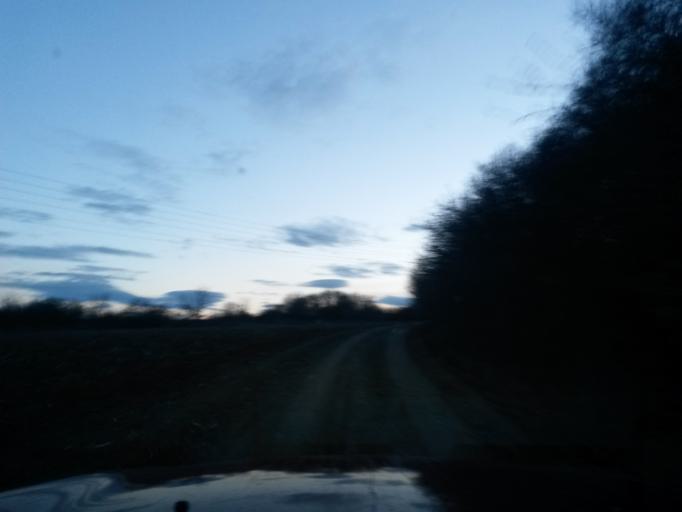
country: SK
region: Kosicky
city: Kosice
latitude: 48.6904
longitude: 21.3809
